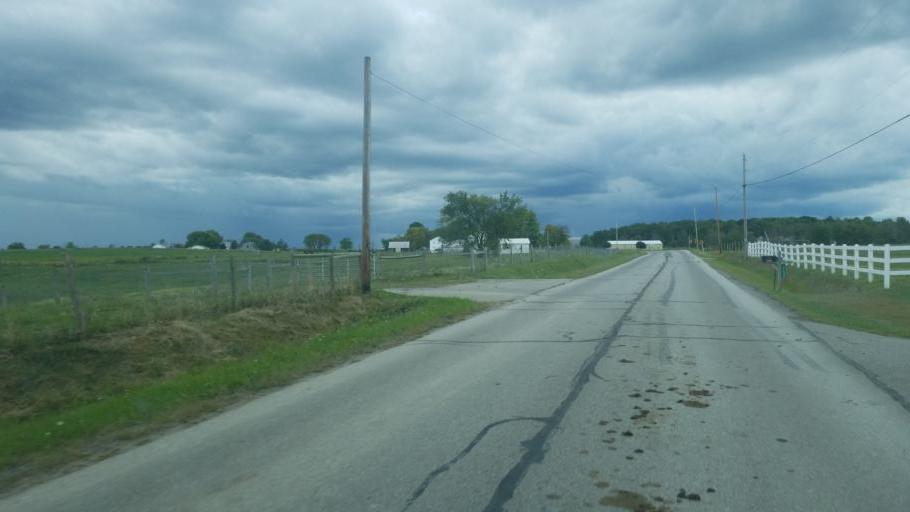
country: US
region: Ohio
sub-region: Geauga County
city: Middlefield
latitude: 41.3866
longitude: -81.0974
